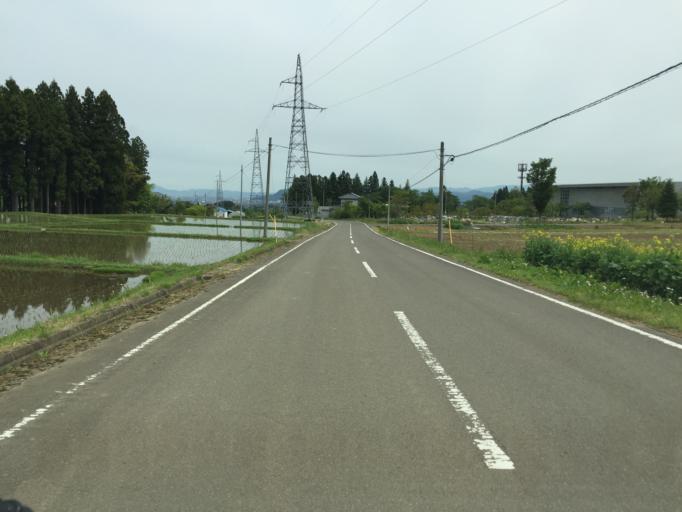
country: JP
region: Fukushima
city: Fukushima-shi
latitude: 37.7102
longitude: 140.3686
